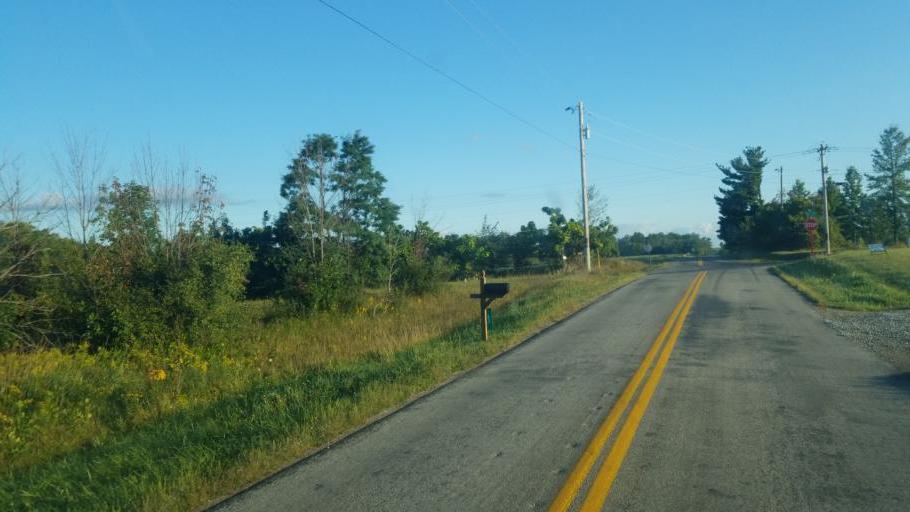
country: US
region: Ohio
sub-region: Lorain County
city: Wellington
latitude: 41.0571
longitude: -82.2586
